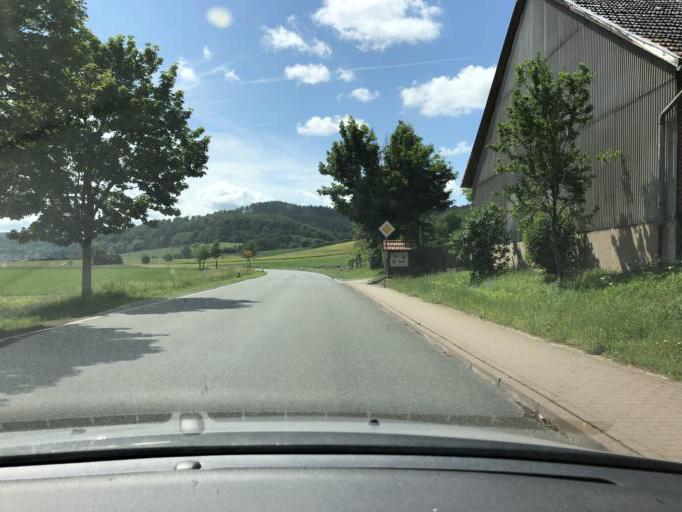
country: DE
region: Hesse
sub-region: Regierungsbezirk Kassel
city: Alheim
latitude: 51.0195
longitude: 9.6706
